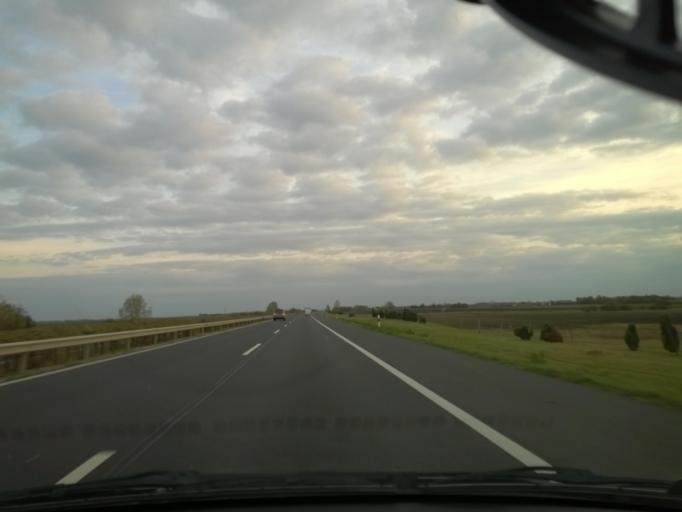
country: HU
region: Bacs-Kiskun
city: Fueloepjakab
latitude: 46.7443
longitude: 19.7802
